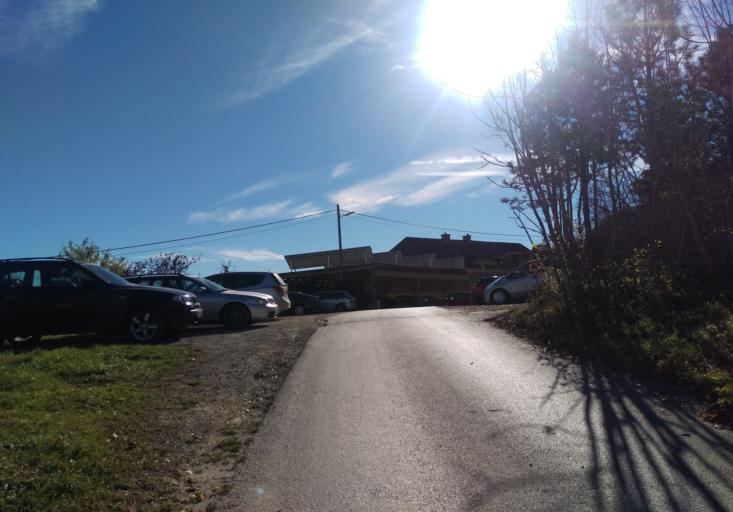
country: AT
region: Styria
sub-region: Graz Stadt
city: Mariatrost
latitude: 47.1246
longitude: 15.4950
